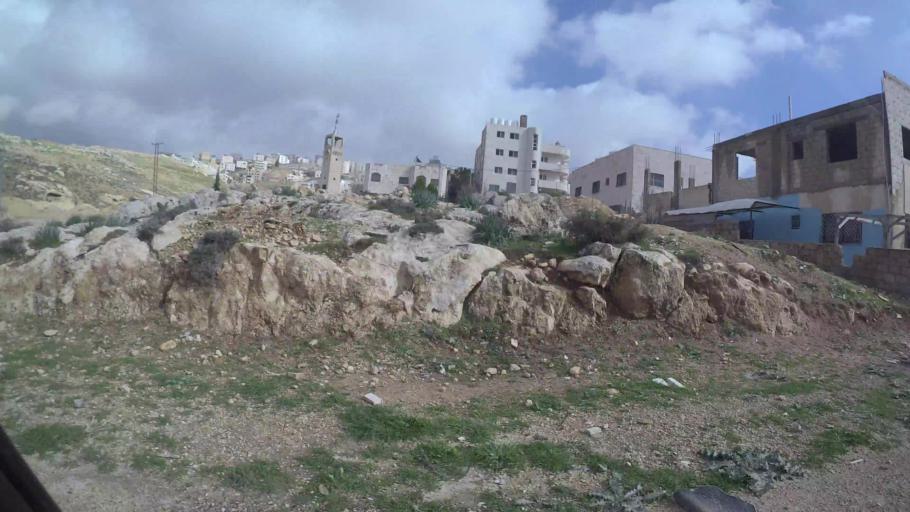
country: JO
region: Amman
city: Al Jubayhah
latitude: 32.0618
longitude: 35.8614
